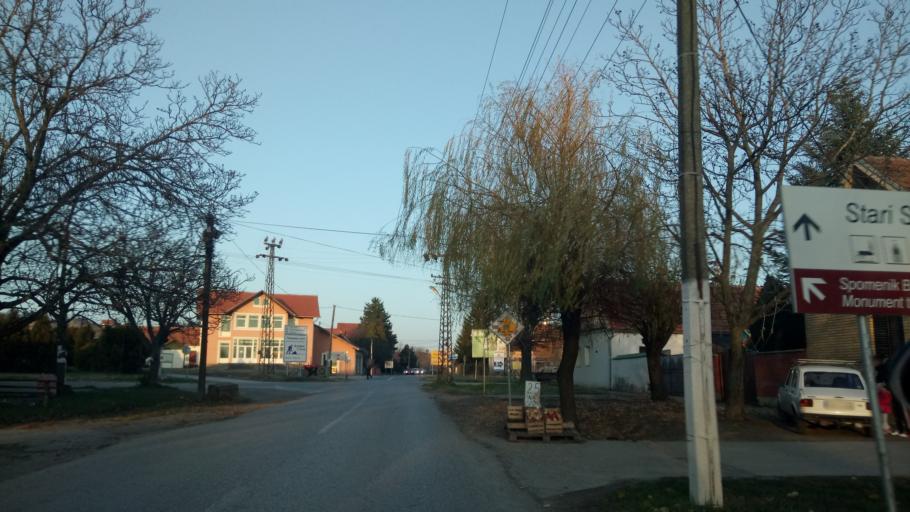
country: RS
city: Novi Slankamen
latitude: 45.1339
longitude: 20.2498
